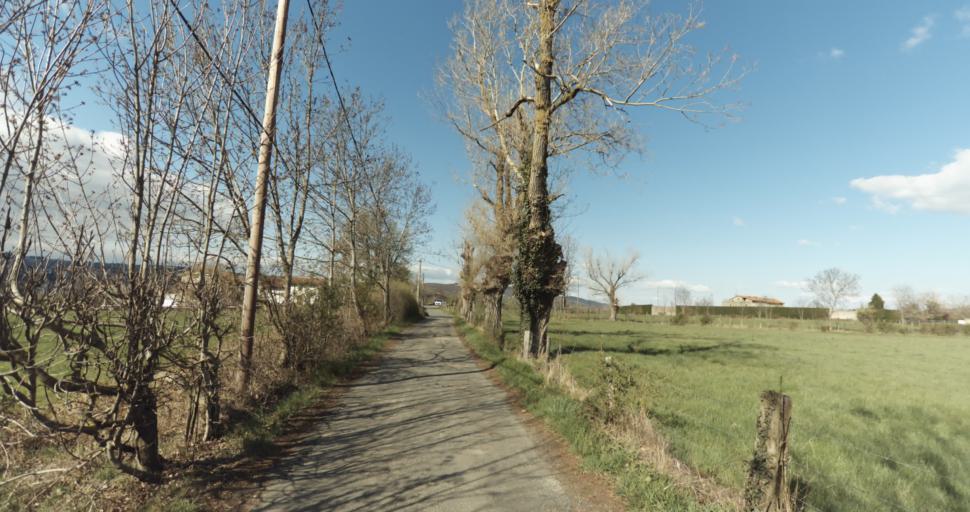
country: FR
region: Rhone-Alpes
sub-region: Departement de la Loire
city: Sorbiers
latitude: 45.4721
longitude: 4.4572
